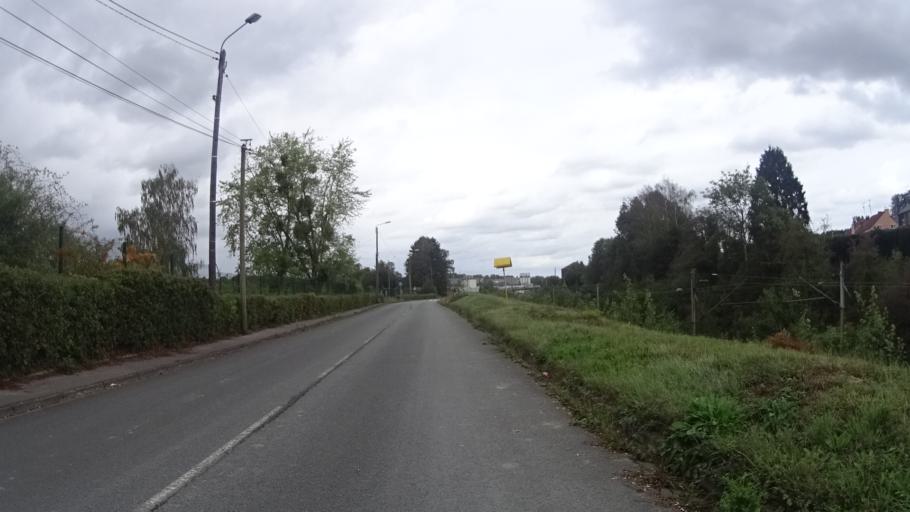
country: FR
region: Nord-Pas-de-Calais
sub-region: Departement du Nord
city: Hautmont
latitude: 50.2414
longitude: 3.8958
